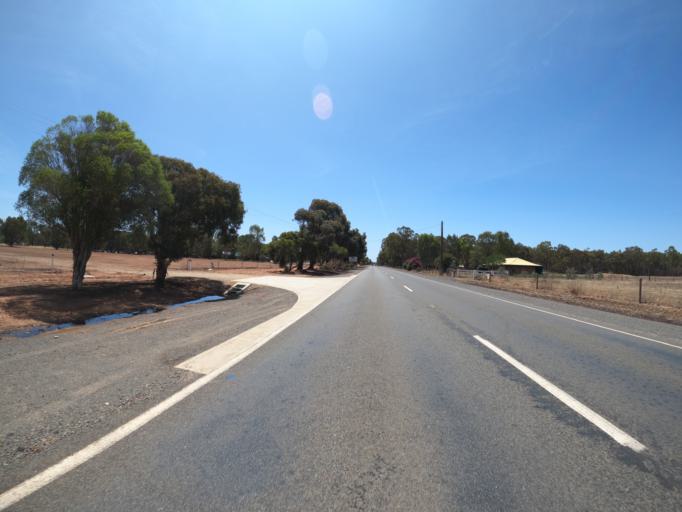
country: AU
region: Victoria
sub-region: Moira
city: Yarrawonga
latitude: -36.0383
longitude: 145.9955
